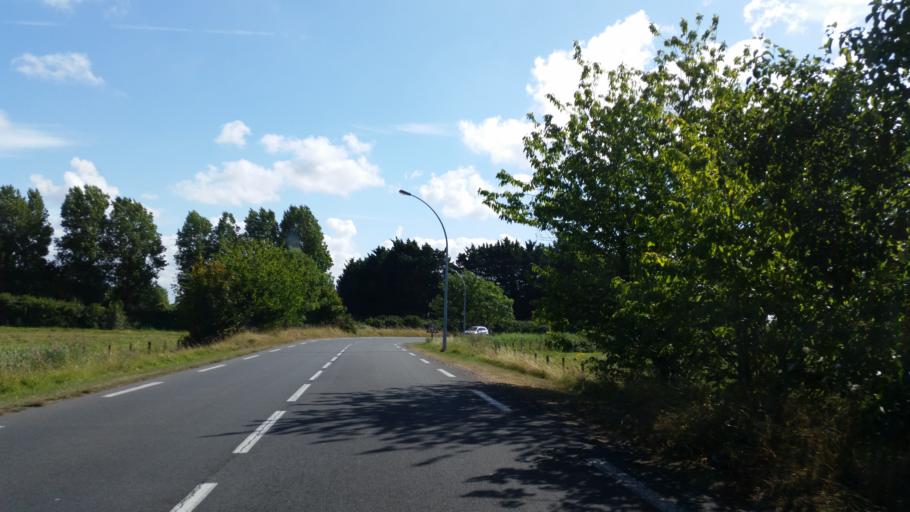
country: FR
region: Lower Normandy
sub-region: Departement du Calvados
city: Ouistreham
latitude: 49.2719
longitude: -0.2534
